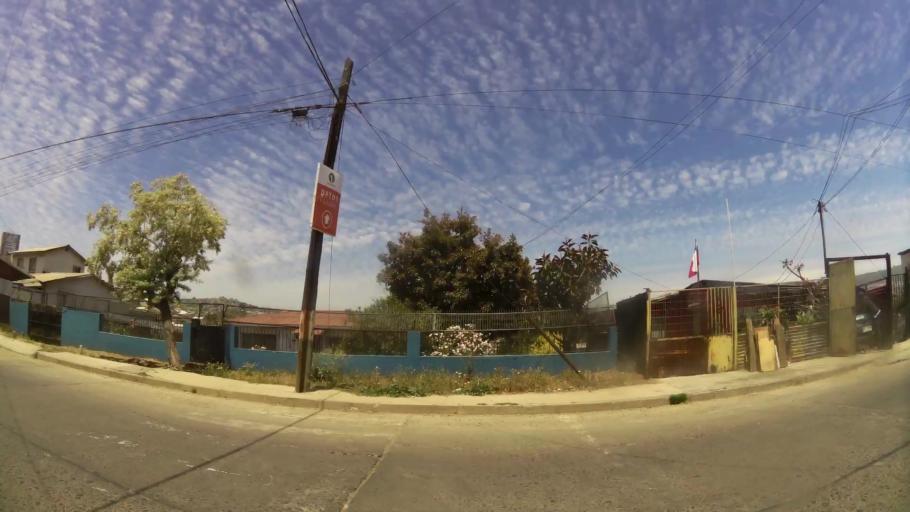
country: CL
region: Valparaiso
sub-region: Provincia de Valparaiso
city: Vina del Mar
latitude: -33.0455
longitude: -71.5864
